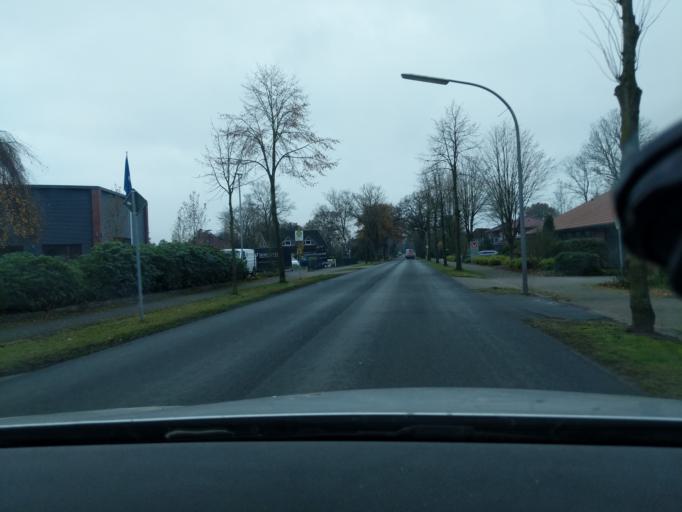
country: DE
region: Lower Saxony
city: Heeslingen
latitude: 53.3205
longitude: 9.3424
